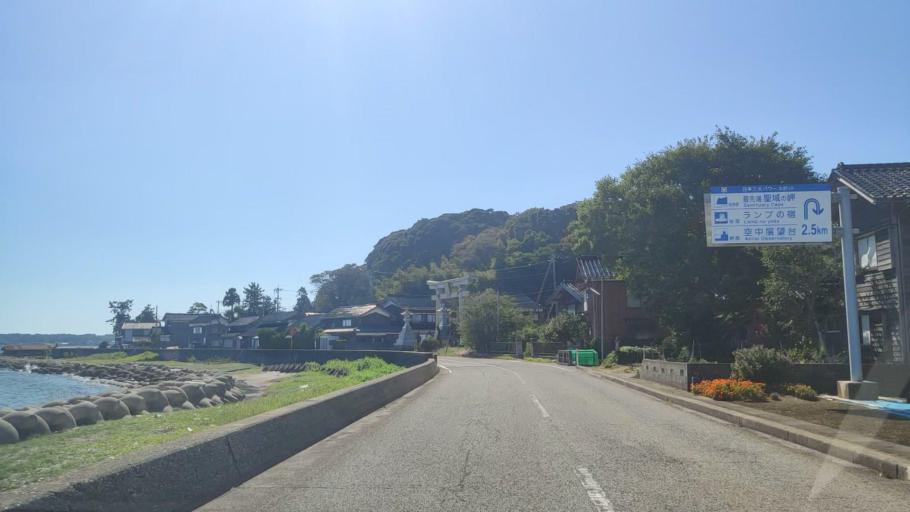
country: JP
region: Toyama
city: Nyuzen
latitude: 37.4965
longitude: 137.3475
